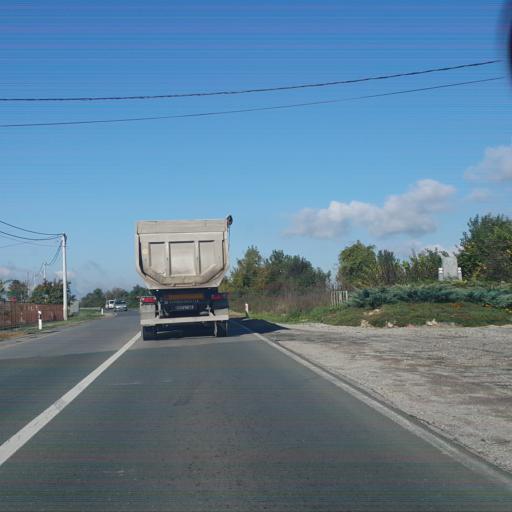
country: RS
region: Central Serbia
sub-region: Rasinski Okrug
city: Trstenik
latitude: 43.6323
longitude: 20.9615
